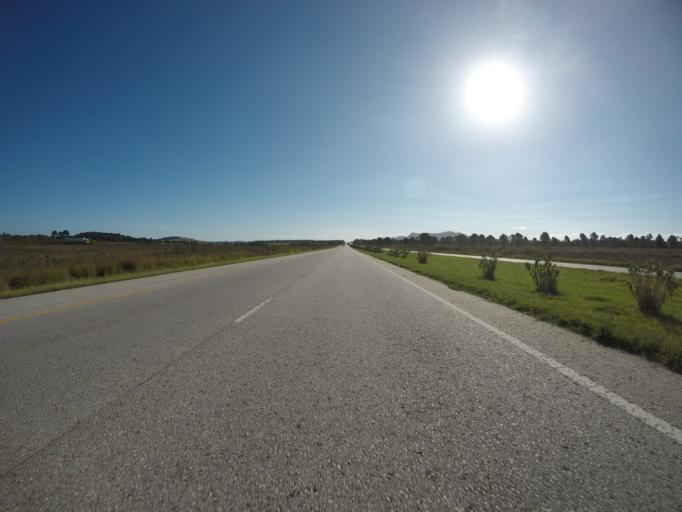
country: ZA
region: Eastern Cape
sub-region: Nelson Mandela Bay Metropolitan Municipality
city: Uitenhage
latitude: -33.9301
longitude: 25.3405
